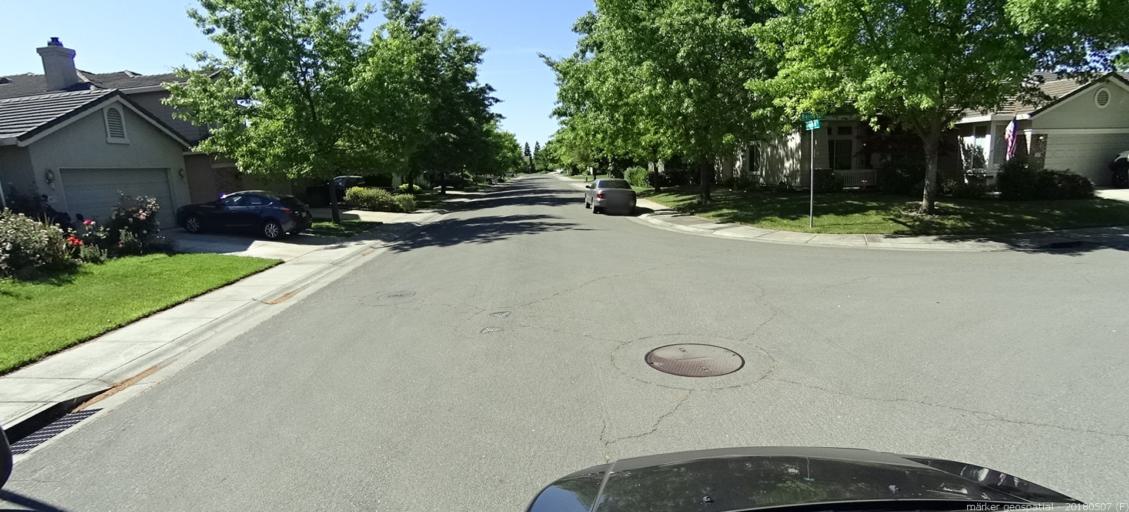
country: US
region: California
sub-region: Sacramento County
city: Rio Linda
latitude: 38.6619
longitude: -121.4938
